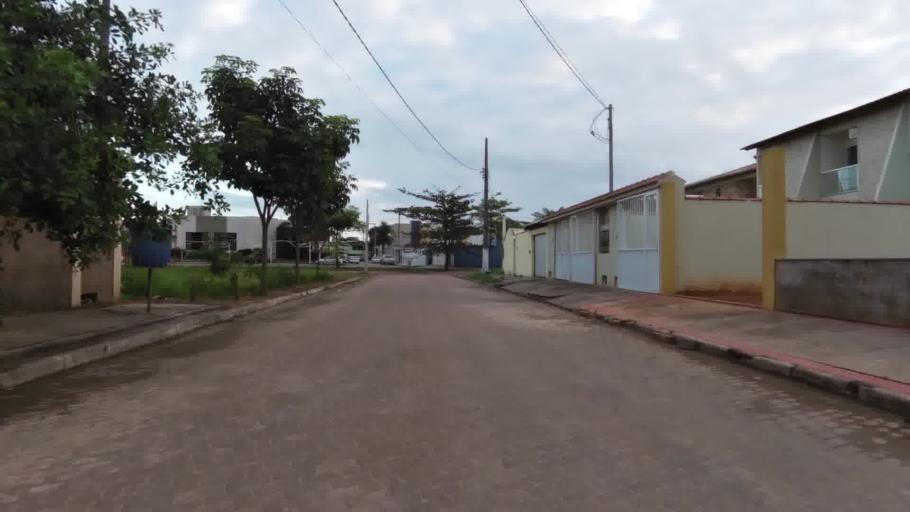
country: BR
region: Espirito Santo
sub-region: Piuma
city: Piuma
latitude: -20.8123
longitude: -40.6310
